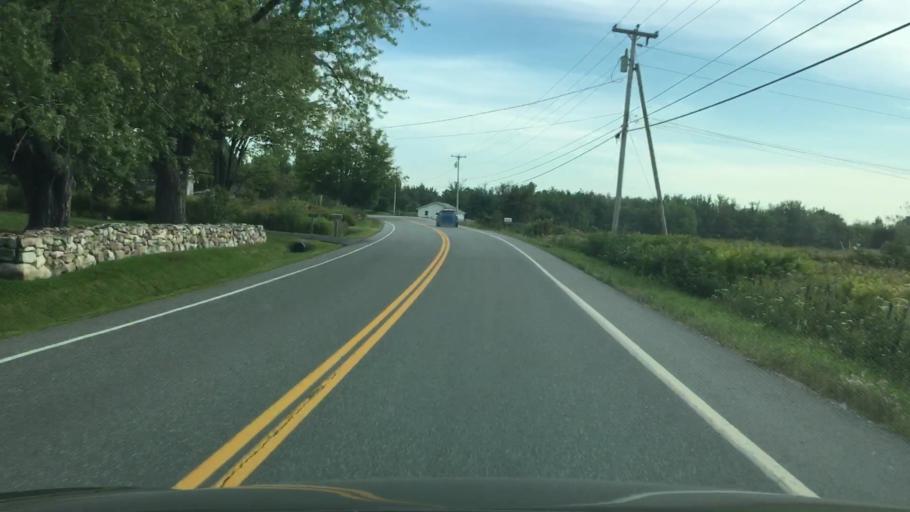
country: US
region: Maine
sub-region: Hancock County
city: Penobscot
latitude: 44.4719
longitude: -68.7812
